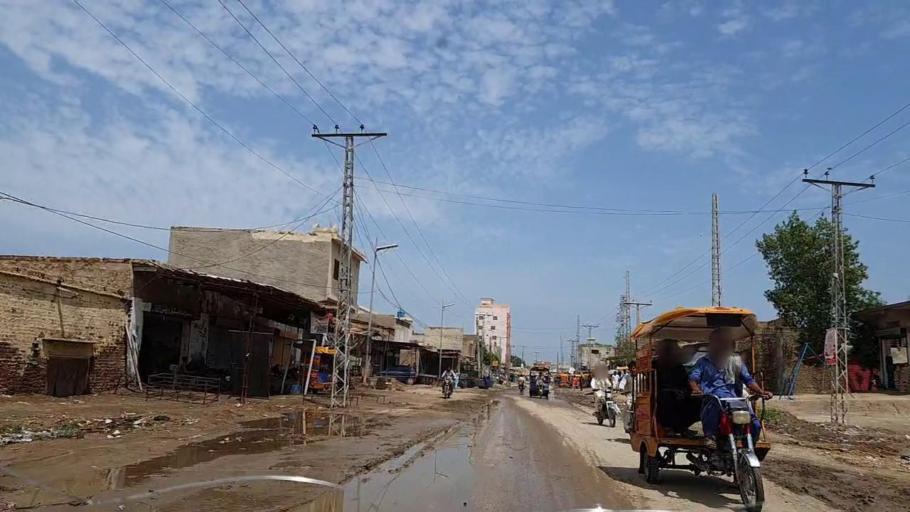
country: PK
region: Sindh
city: Naushahro Firoz
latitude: 26.8425
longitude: 68.1159
